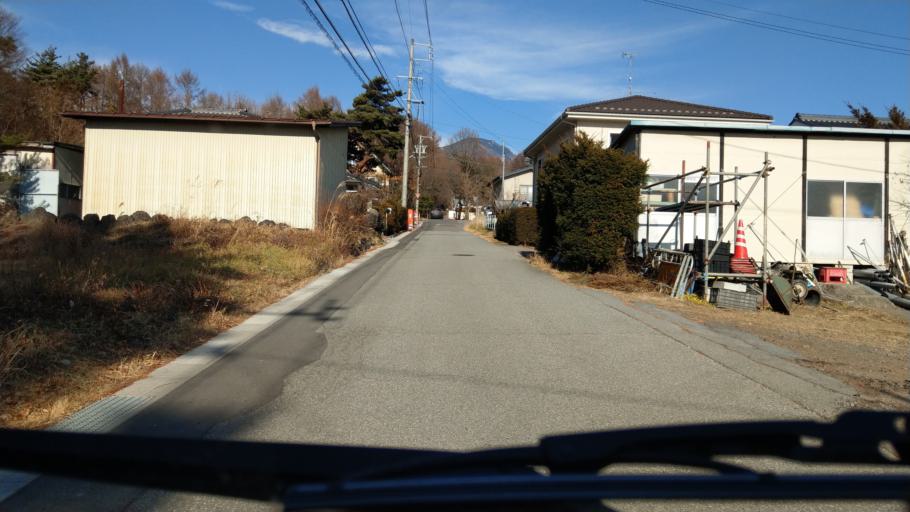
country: JP
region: Nagano
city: Komoro
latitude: 36.3384
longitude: 138.4517
